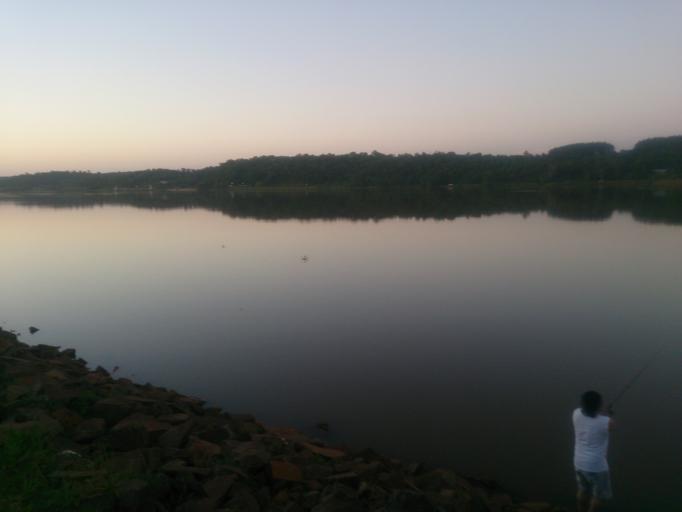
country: PY
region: Itapua
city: Bella Vista
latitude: -27.1063
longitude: -55.5217
